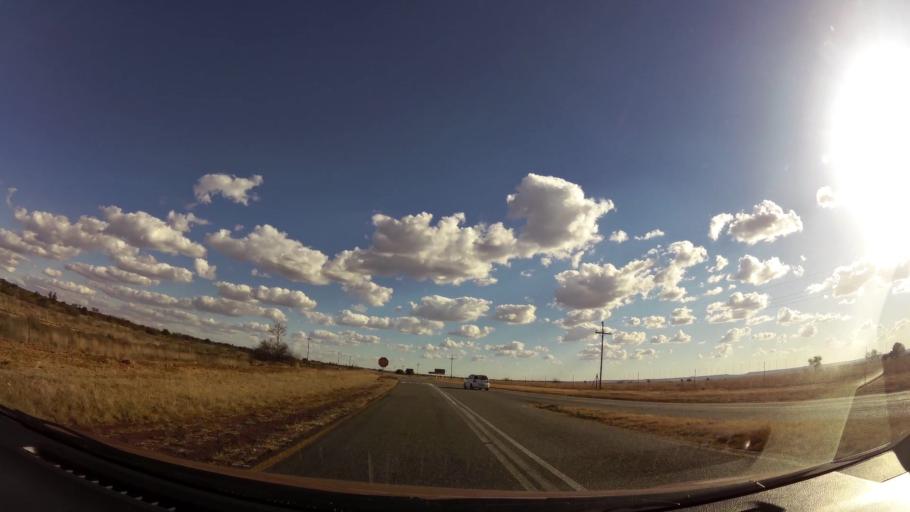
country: ZA
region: Gauteng
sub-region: West Rand District Municipality
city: Carletonville
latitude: -26.4136
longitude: 27.2350
